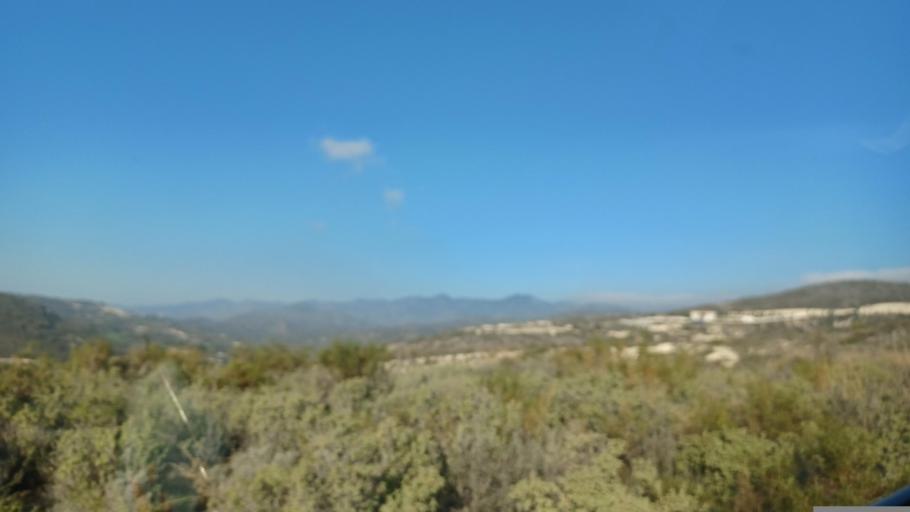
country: CY
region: Larnaka
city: Kofinou
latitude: 34.8368
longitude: 33.3026
